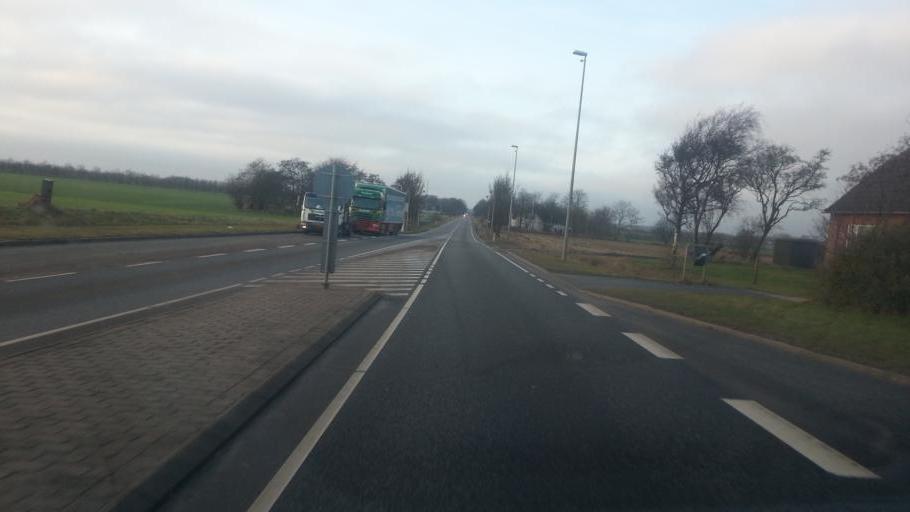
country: DK
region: South Denmark
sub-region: Esbjerg Kommune
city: Bramming
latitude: 55.4877
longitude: 8.6397
